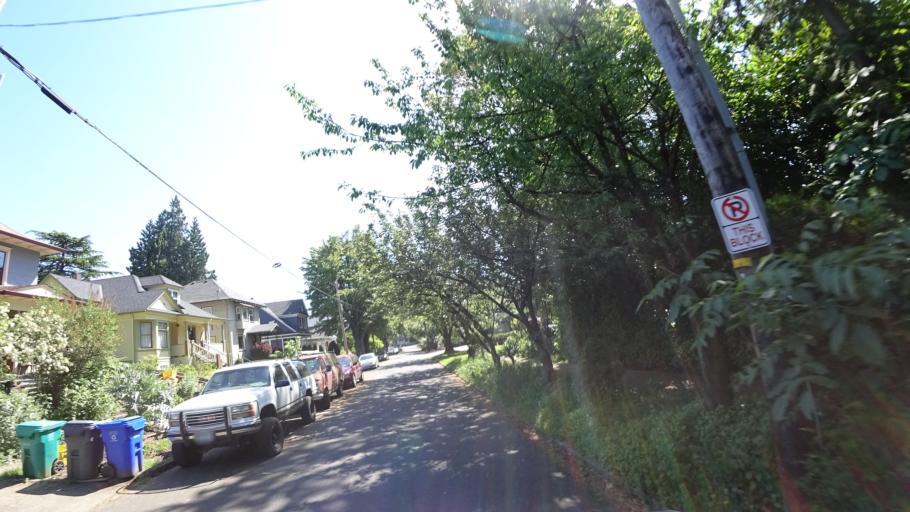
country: US
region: Oregon
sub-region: Multnomah County
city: Portland
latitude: 45.5314
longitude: -122.6407
